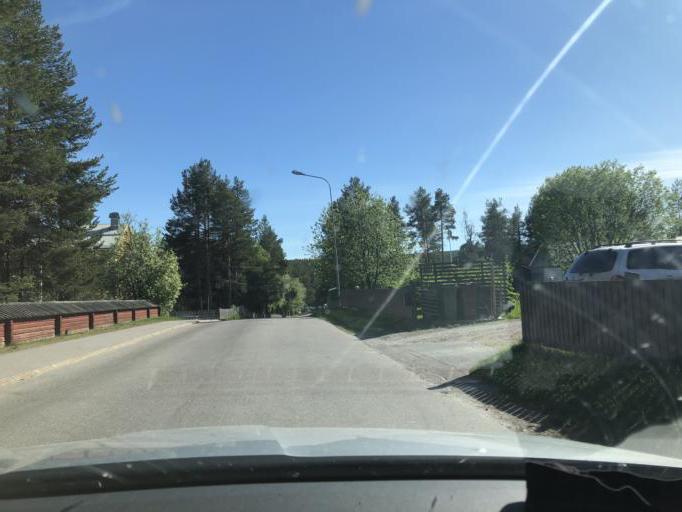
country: SE
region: Norrbotten
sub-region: Jokkmokks Kommun
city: Jokkmokk
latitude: 66.6042
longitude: 19.8298
